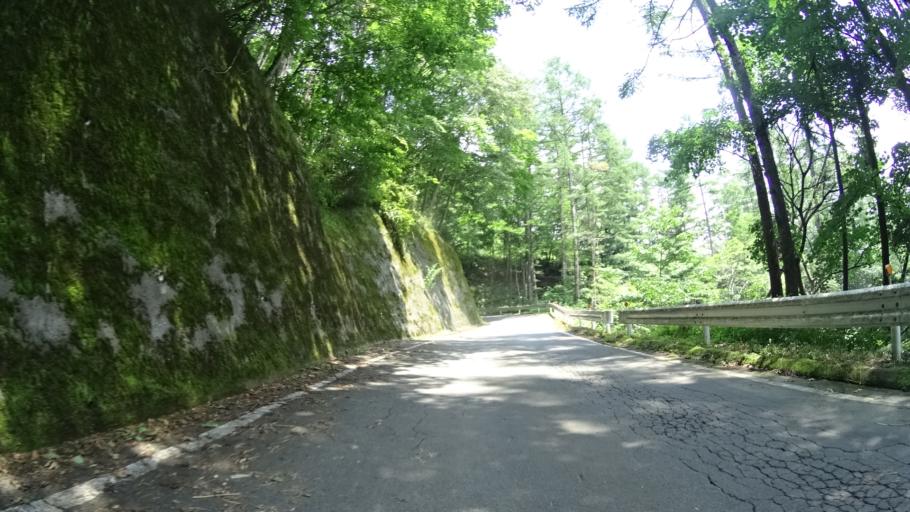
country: JP
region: Nagano
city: Saku
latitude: 36.1037
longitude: 138.6467
